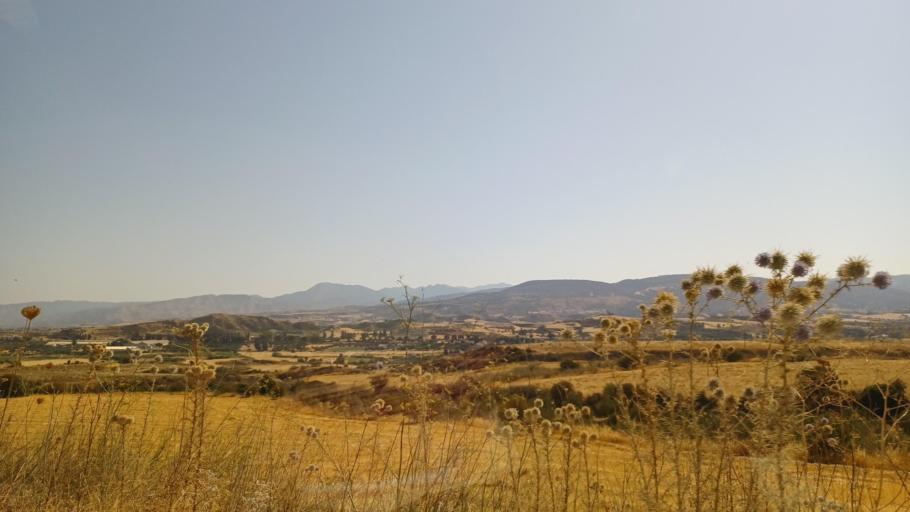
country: CY
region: Pafos
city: Polis
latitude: 35.0132
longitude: 32.4189
